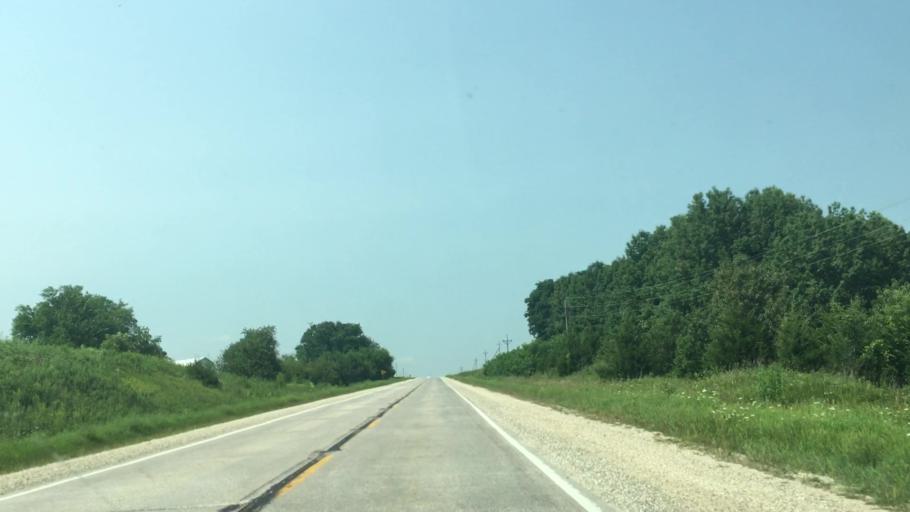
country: US
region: Iowa
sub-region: Fayette County
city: West Union
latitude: 43.0855
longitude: -91.8482
